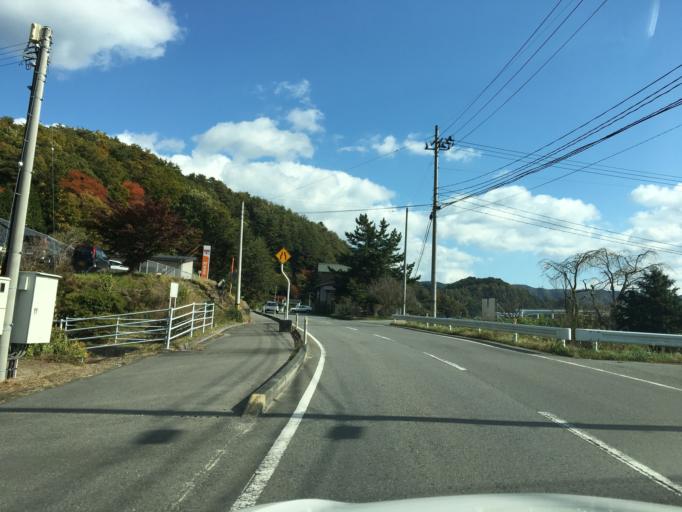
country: JP
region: Fukushima
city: Namie
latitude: 37.3292
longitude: 140.8233
